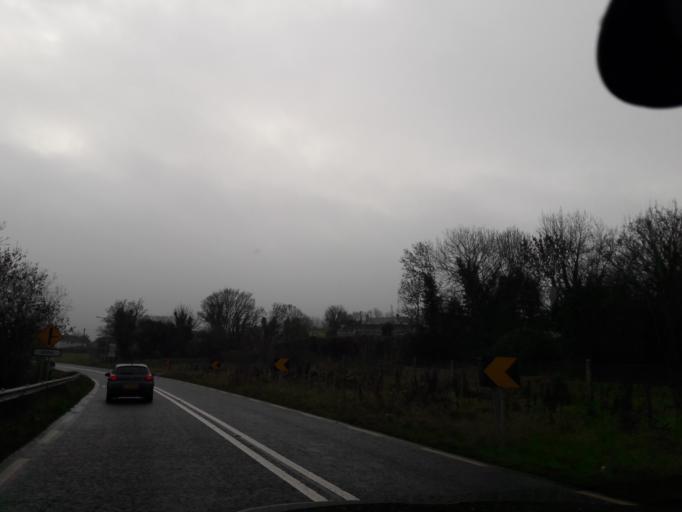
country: IE
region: Ulster
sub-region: County Donegal
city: Leifear
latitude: 54.8429
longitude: -7.4984
